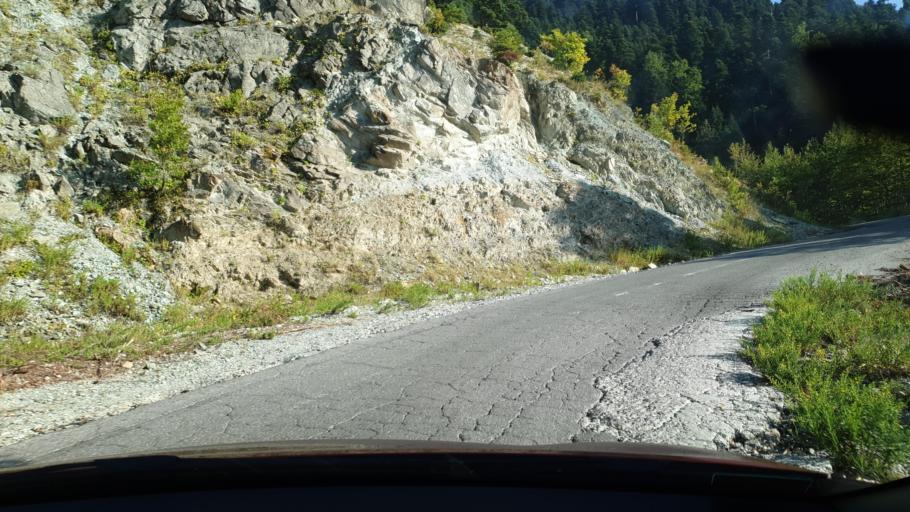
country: GR
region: Central Greece
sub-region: Nomos Evvoias
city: Yimnon
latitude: 38.6066
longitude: 23.9209
